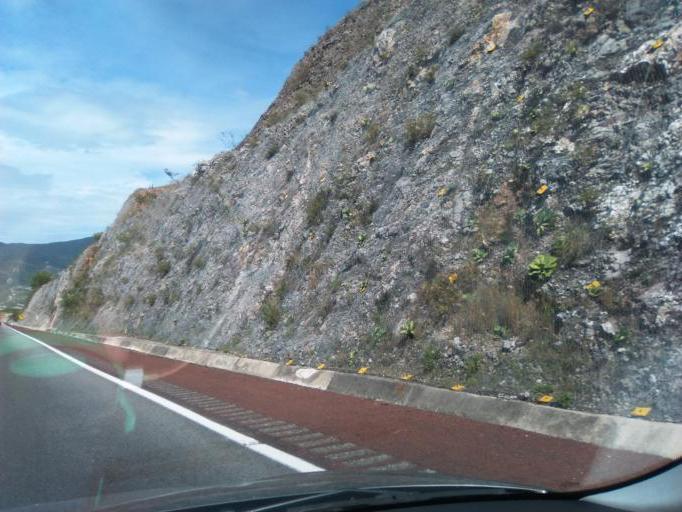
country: MX
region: Guerrero
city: Petaquillas
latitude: 17.4700
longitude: -99.4724
